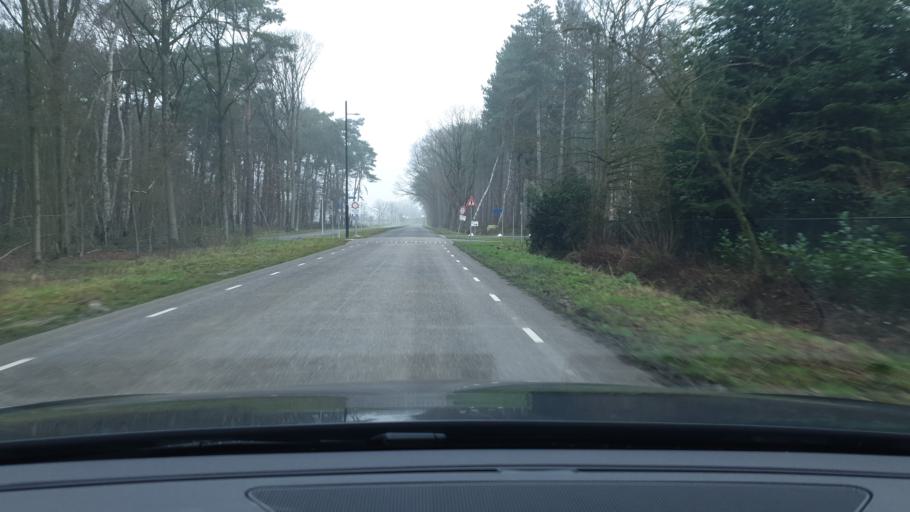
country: NL
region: North Brabant
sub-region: Gemeente Eindhoven
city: Meerhoven
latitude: 51.4643
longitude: 5.4015
